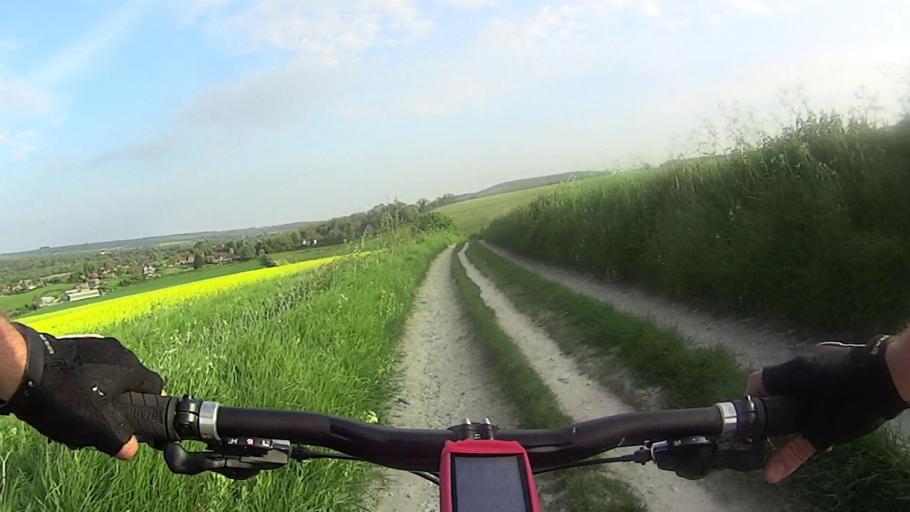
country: GB
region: England
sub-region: West Sussex
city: Arundel
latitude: 50.8982
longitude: -0.5607
